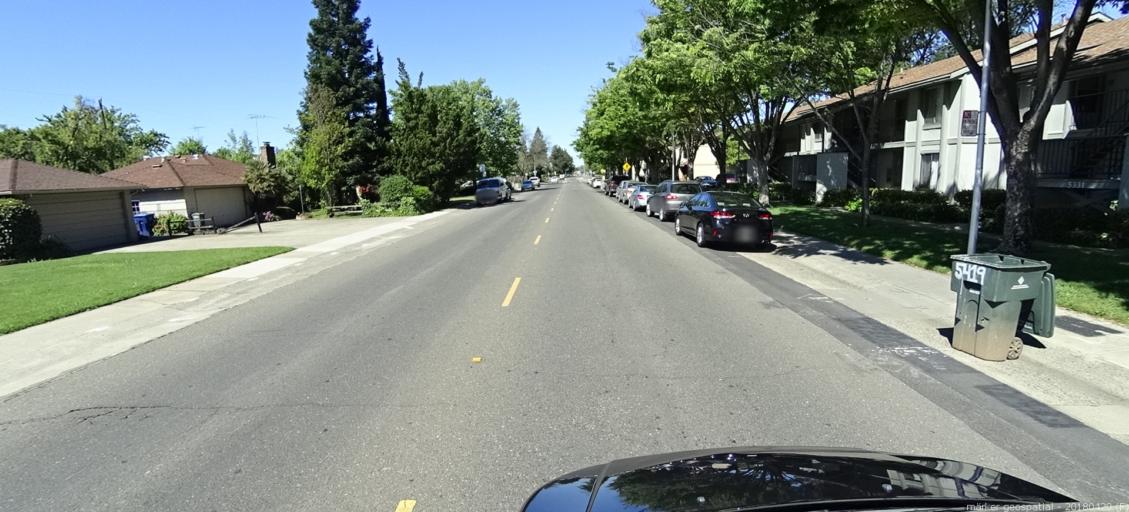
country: US
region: California
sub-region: Sacramento County
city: Parkway
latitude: 38.5467
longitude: -121.4424
